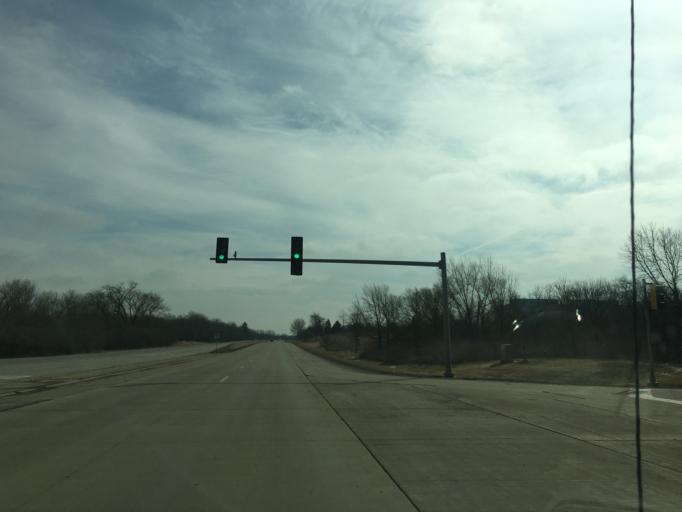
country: US
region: Illinois
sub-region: Kane County
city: East Dundee
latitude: 42.0809
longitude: -88.2204
